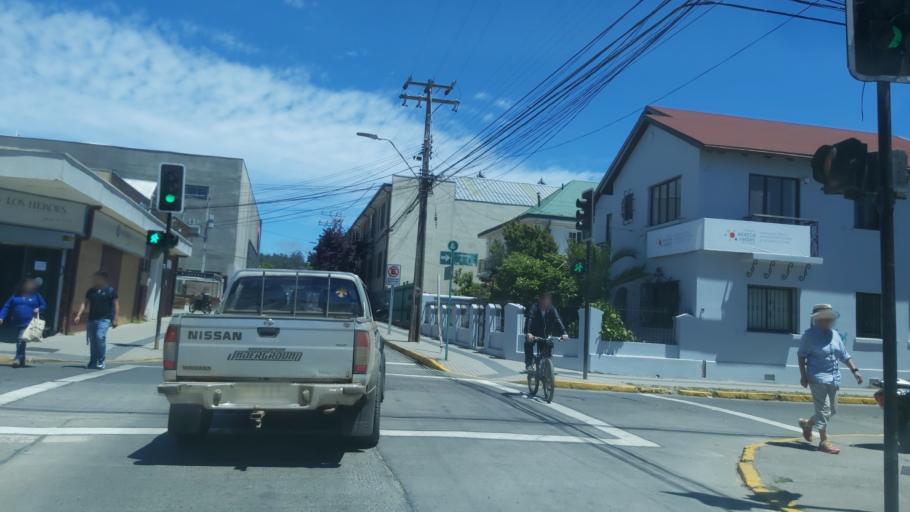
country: CL
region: Maule
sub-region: Provincia de Talca
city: Constitucion
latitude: -35.3295
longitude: -72.4108
